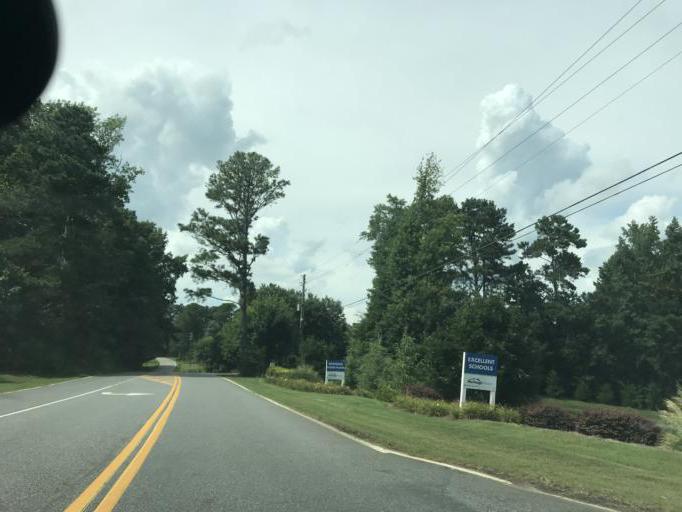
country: US
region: Georgia
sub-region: Forsyth County
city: Cumming
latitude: 34.2291
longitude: -84.2427
